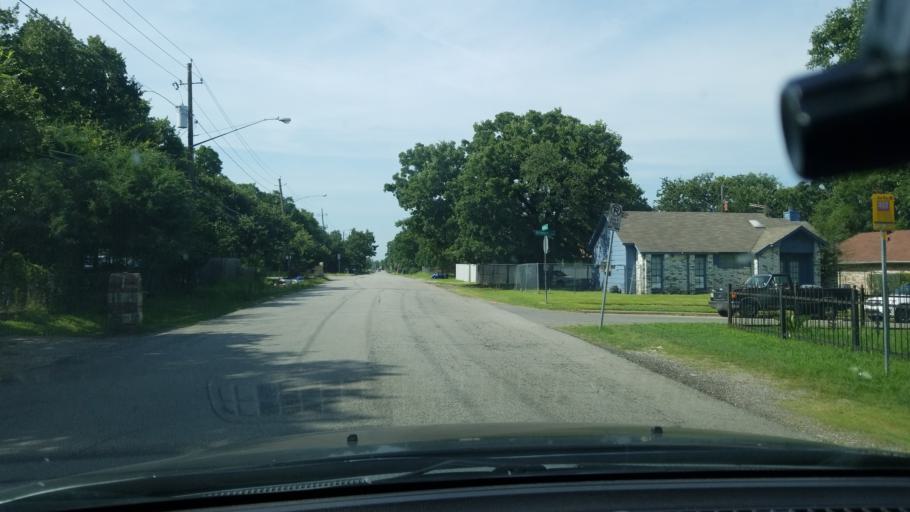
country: US
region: Texas
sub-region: Dallas County
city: Balch Springs
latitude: 32.7302
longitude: -96.6392
